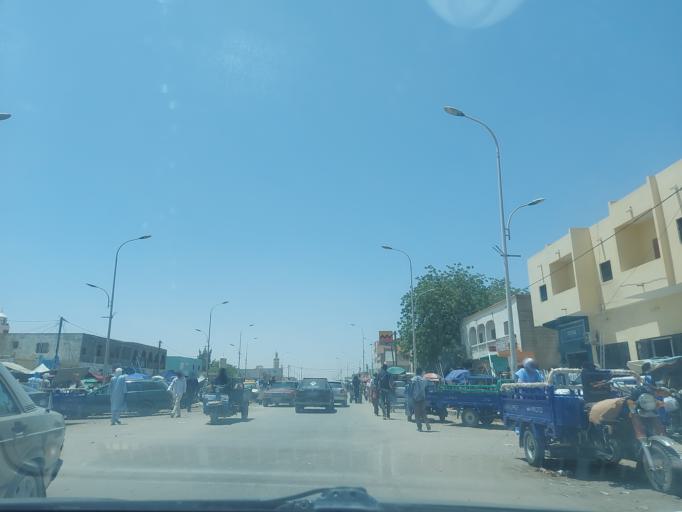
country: MR
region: Nouakchott
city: Nouakchott
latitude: 18.0834
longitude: -15.9812
